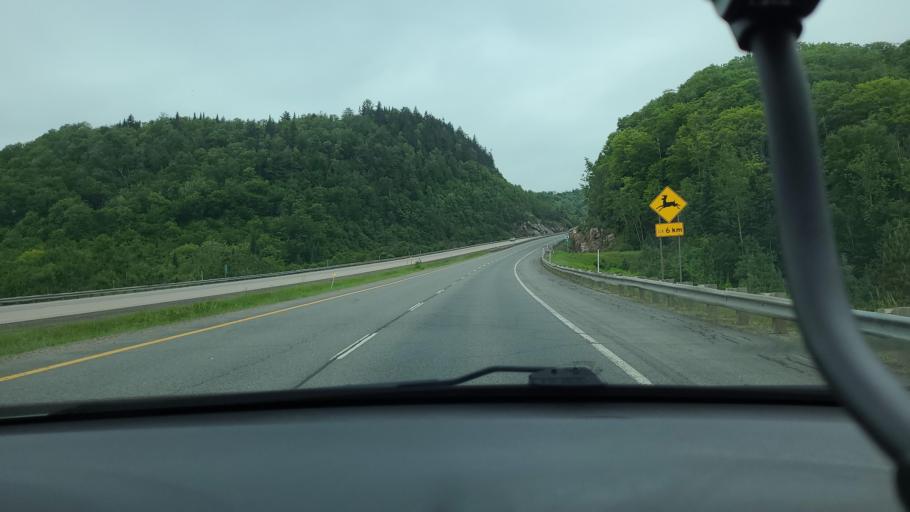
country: CA
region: Quebec
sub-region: Laurentides
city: Mont-Tremblant
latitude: 46.1459
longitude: -74.6569
